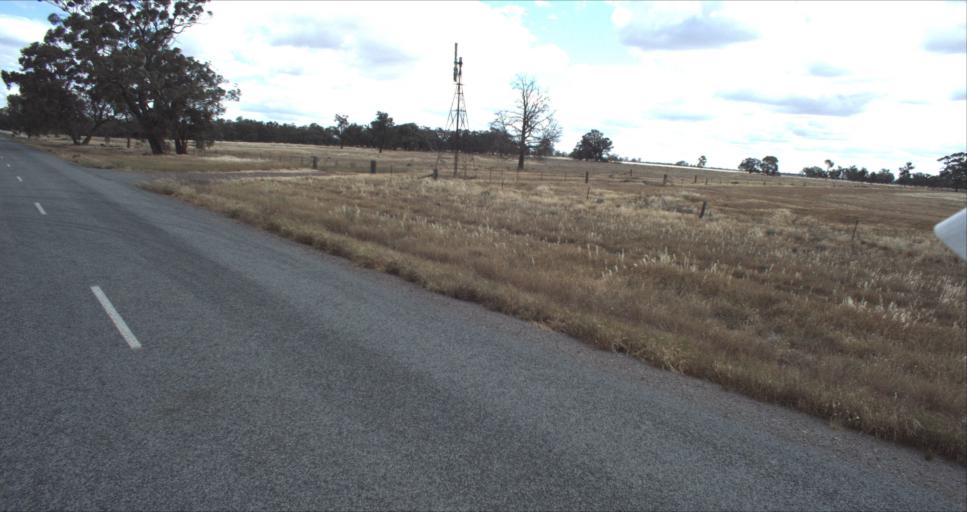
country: AU
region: New South Wales
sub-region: Leeton
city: Leeton
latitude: -34.6861
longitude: 146.3446
